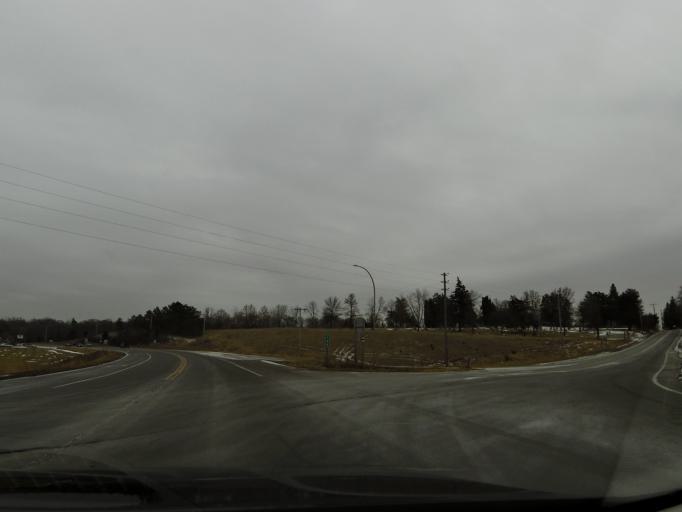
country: US
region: Minnesota
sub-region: Hennepin County
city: Independence
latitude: 45.0103
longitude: -93.6868
